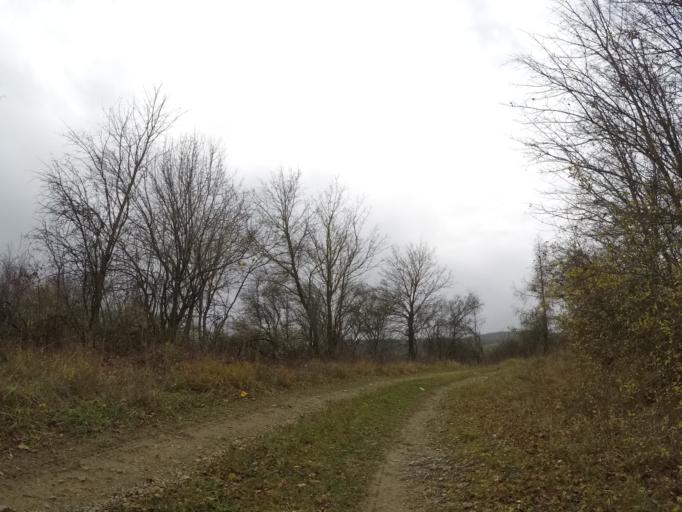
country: SK
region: Presovsky
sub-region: Okres Presov
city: Presov
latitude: 48.9039
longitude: 21.1765
